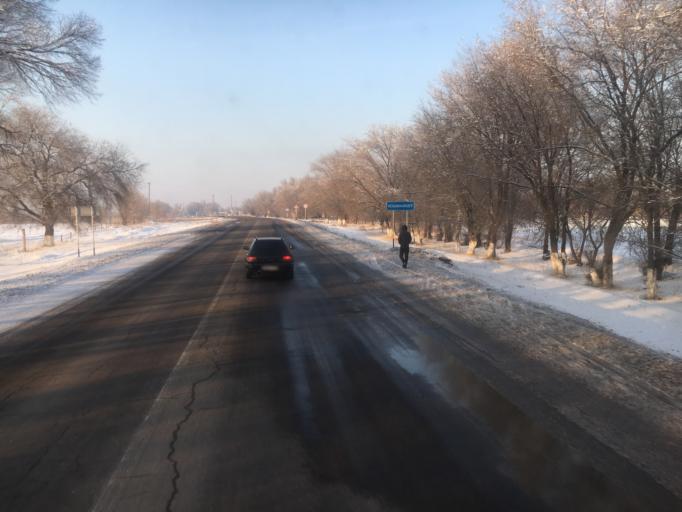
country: KZ
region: Almaty Oblysy
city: Burunday
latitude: 43.3295
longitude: 76.6622
